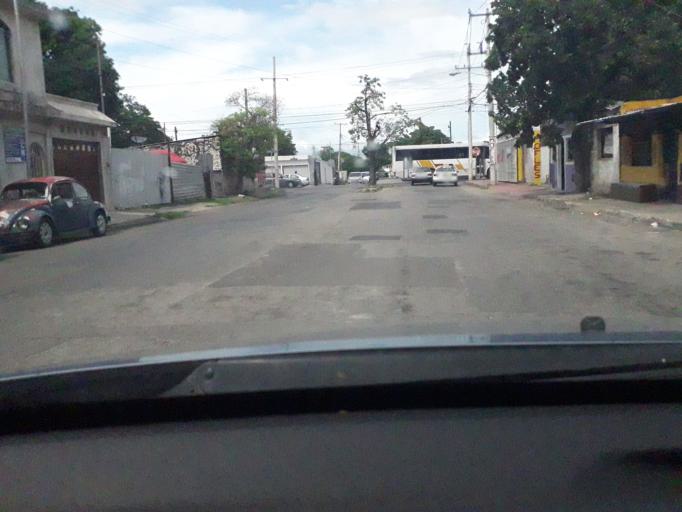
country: MX
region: Yucatan
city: Merida
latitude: 20.9622
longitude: -89.6556
